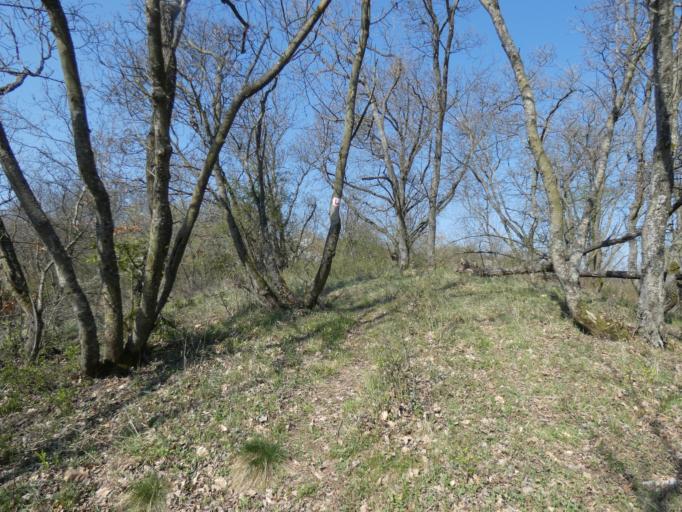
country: HU
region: Pest
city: Szob
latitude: 47.8616
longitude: 18.8546
